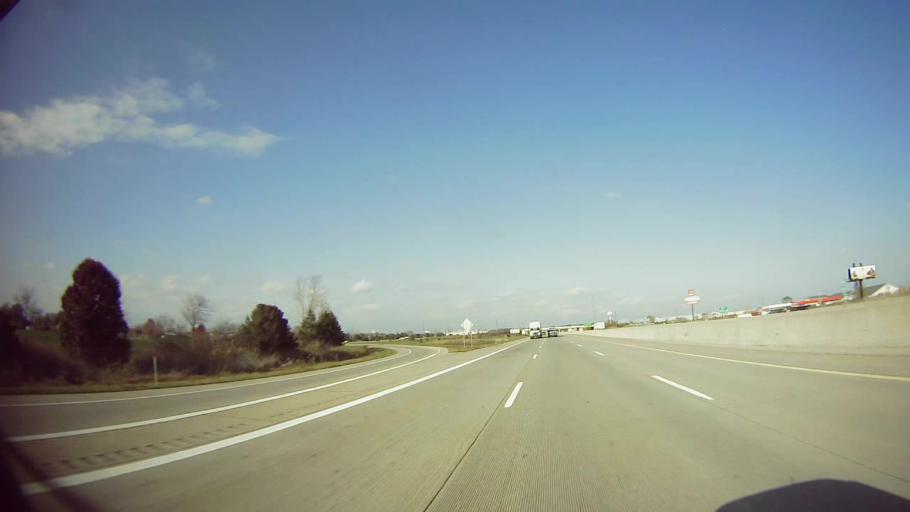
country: US
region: Michigan
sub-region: Wayne County
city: Woodhaven
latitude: 42.1330
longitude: -83.2416
